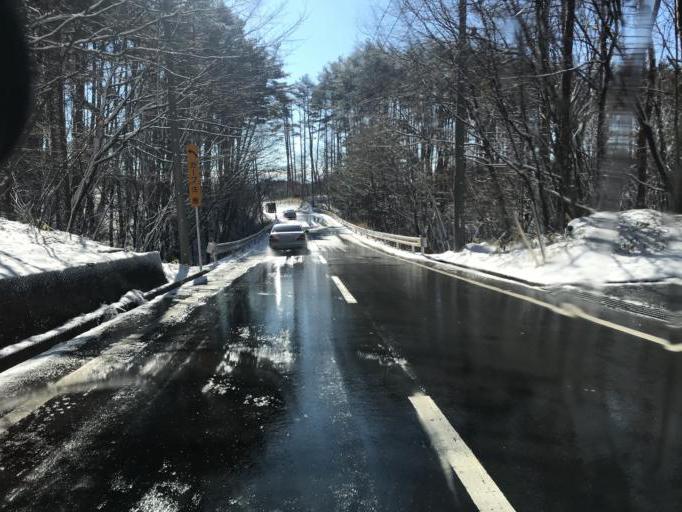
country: JP
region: Yamanashi
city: Nirasaki
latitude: 35.8705
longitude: 138.3284
